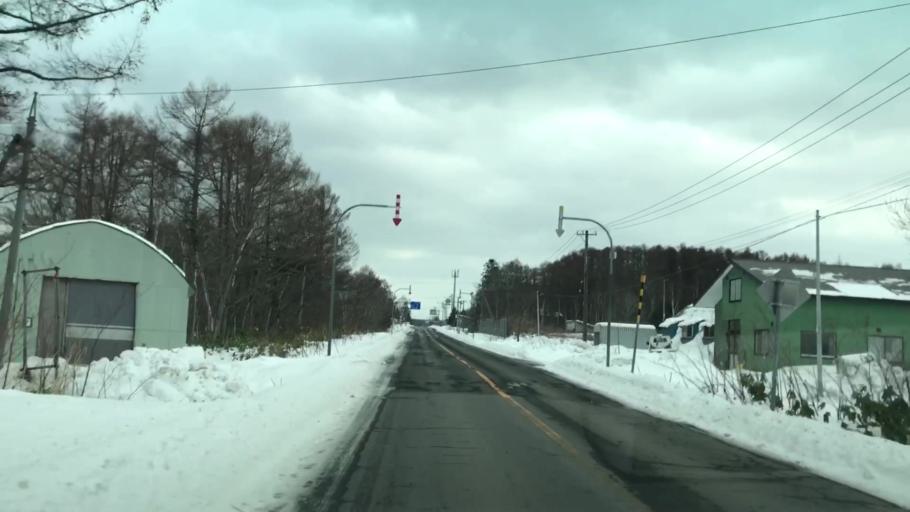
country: JP
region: Hokkaido
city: Yoichi
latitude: 43.3151
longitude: 140.5414
